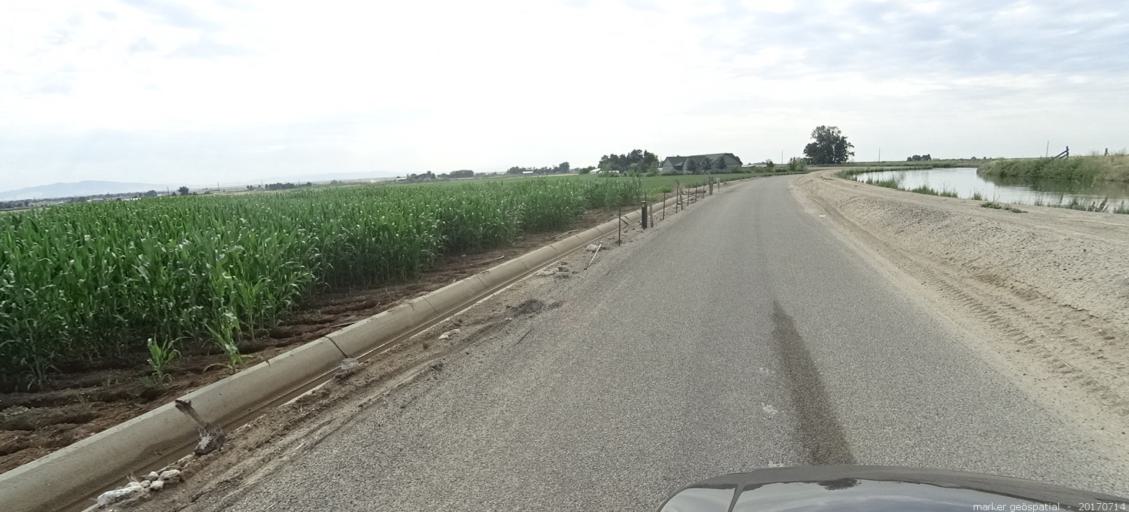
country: US
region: Idaho
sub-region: Ada County
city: Kuna
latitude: 43.4619
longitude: -116.3703
